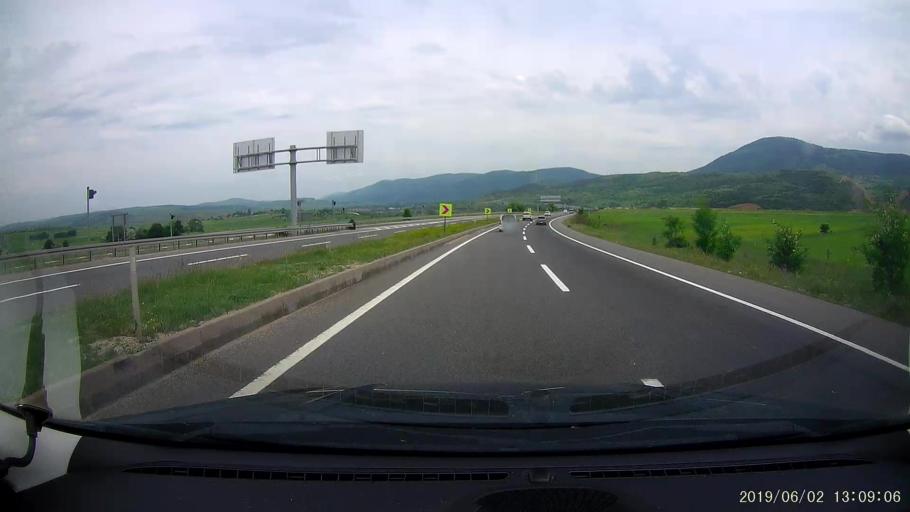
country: TR
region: Karabuk
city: Gozyeri
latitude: 40.8713
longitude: 32.5816
